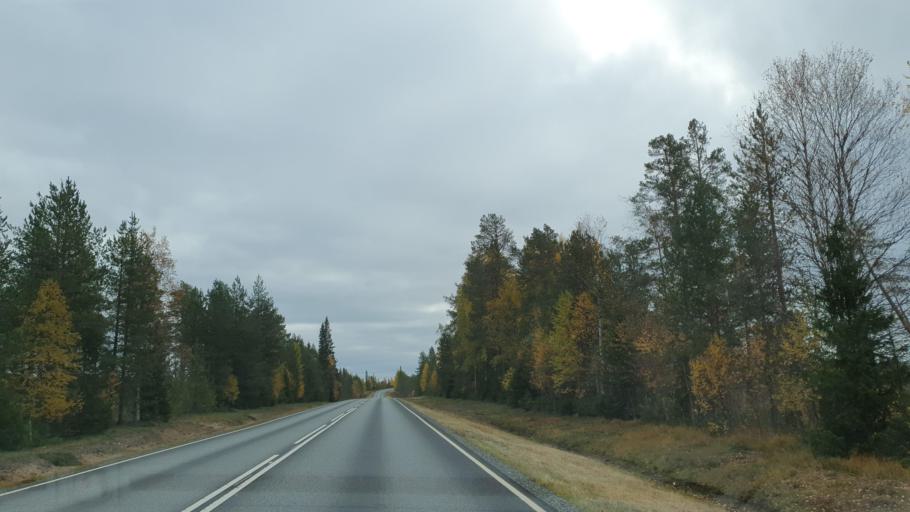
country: FI
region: Lapland
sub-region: Rovaniemi
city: Ranua
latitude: 65.8071
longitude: 26.5605
